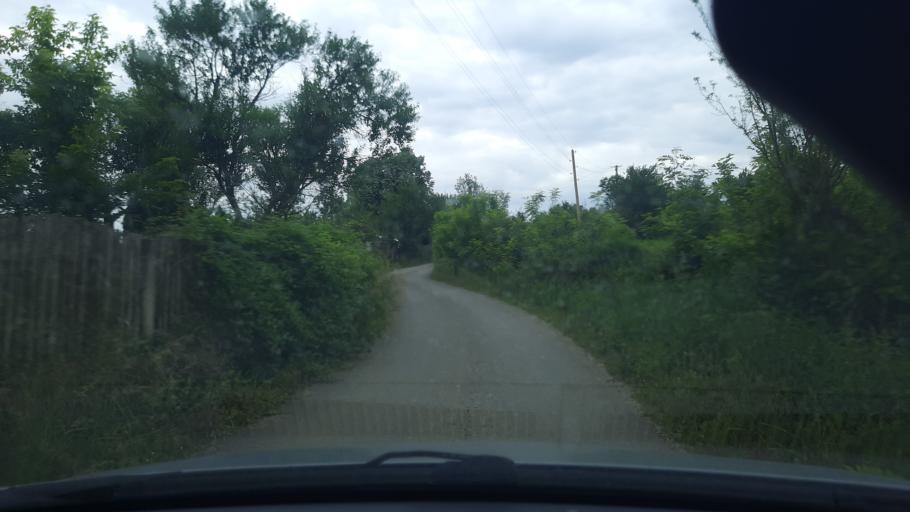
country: RS
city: Jarebice
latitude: 44.5035
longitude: 19.4757
